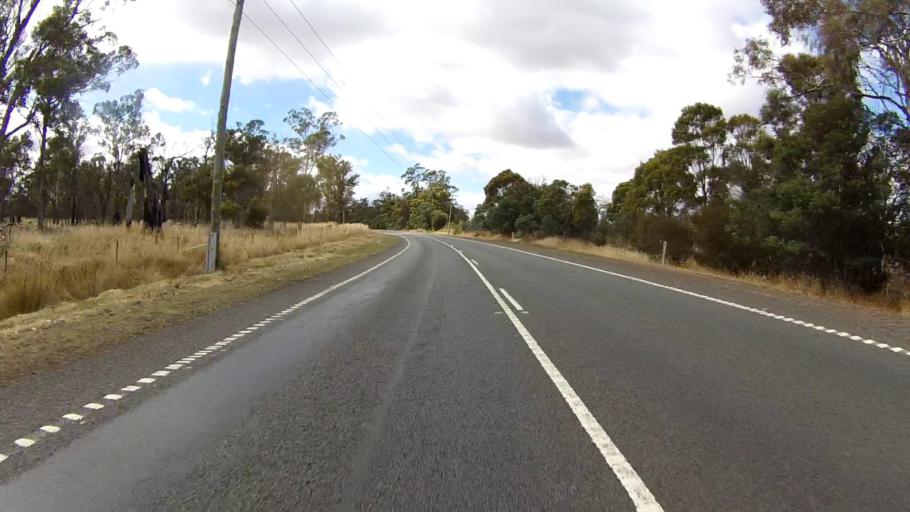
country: AU
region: Tasmania
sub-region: Northern Midlands
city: Evandale
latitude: -41.8253
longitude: 147.4303
